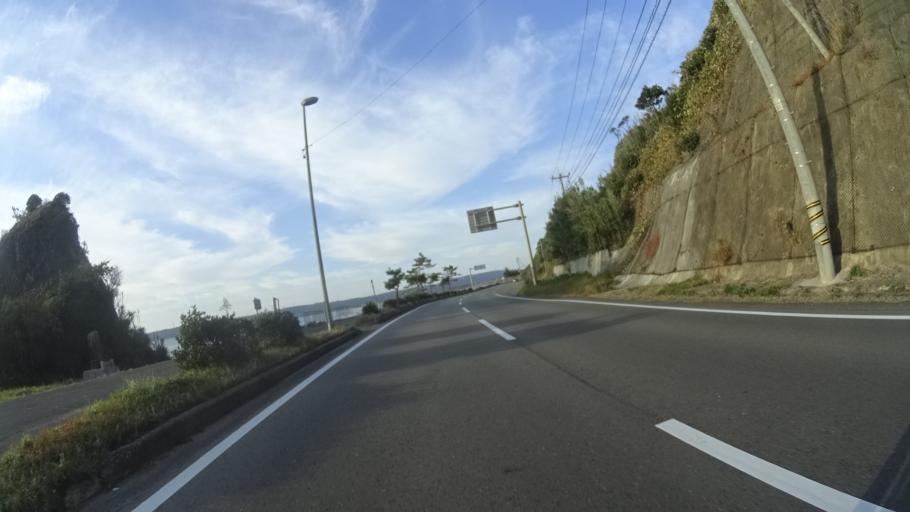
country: JP
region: Ishikawa
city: Hakui
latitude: 37.1286
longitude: 136.7277
